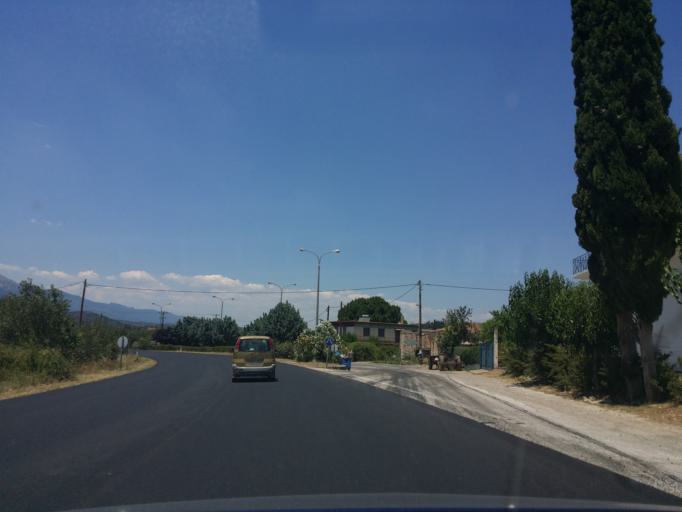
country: GR
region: Peloponnese
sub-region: Nomos Lakonias
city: Sparti
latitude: 37.0873
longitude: 22.4432
